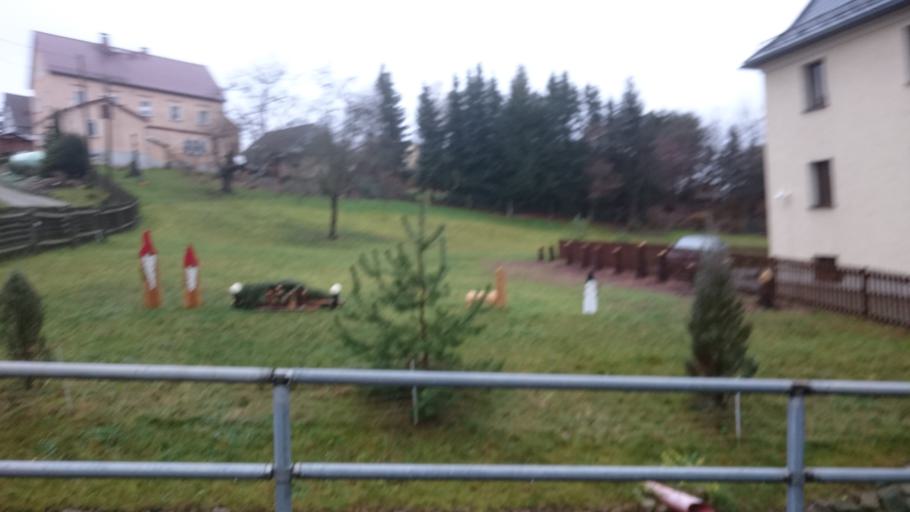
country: DE
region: Saxony
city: Zwickau
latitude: 50.7546
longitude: 12.5194
